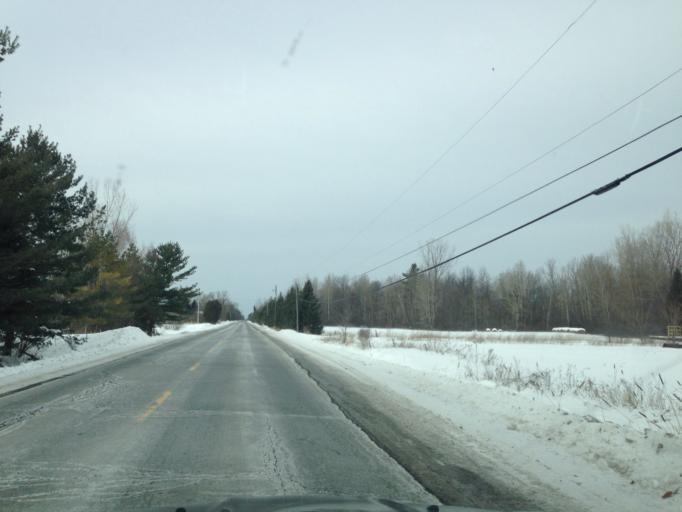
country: CA
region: Ontario
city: Ottawa
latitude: 45.3217
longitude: -75.5399
